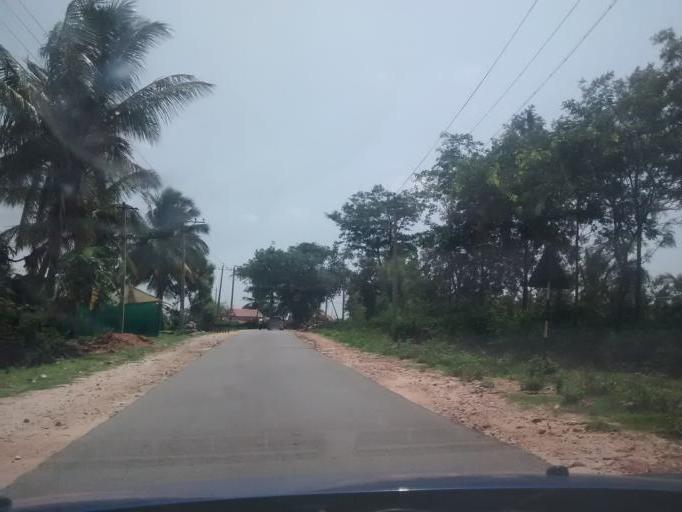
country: IN
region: Karnataka
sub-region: Mandya
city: Krishnarajpet
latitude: 12.5743
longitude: 76.3129
